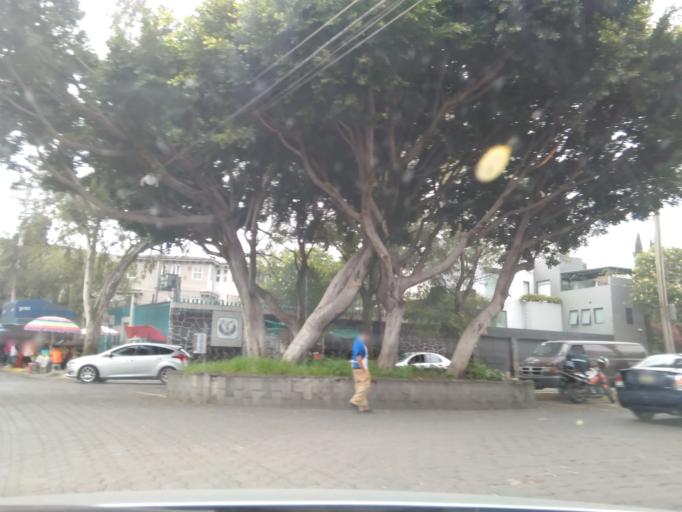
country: MX
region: Mexico City
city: Tlalpan
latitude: 19.2967
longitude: -99.1921
